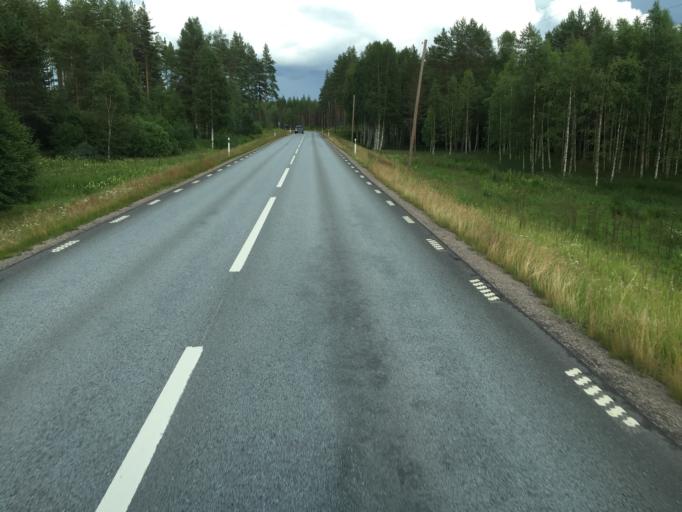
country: SE
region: Dalarna
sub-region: Vansbro Kommun
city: Jarna
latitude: 60.5214
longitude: 14.3004
